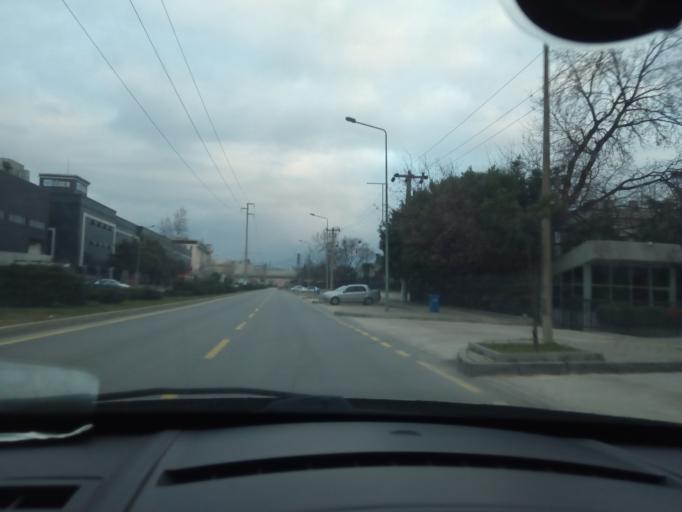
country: TR
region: Bursa
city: Niluefer
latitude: 40.2399
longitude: 28.9658
